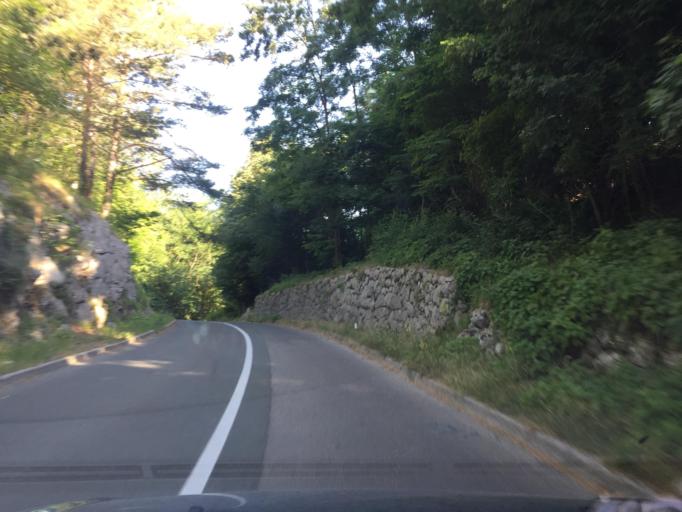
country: HR
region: Primorsko-Goranska
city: Klana
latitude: 45.4373
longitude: 14.3867
